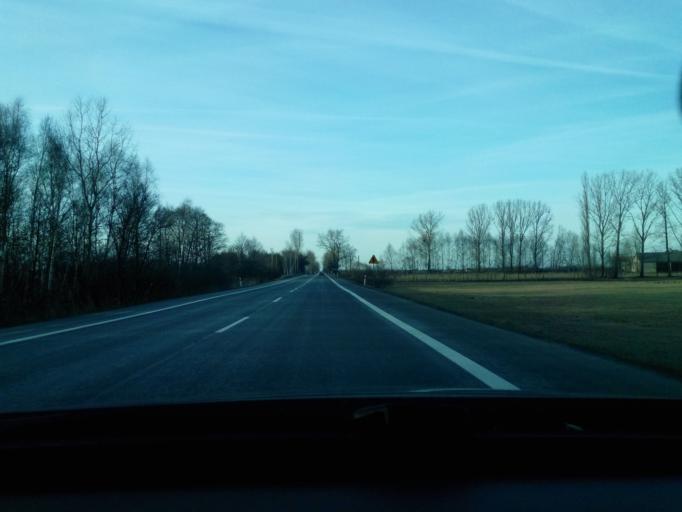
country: PL
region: Kujawsko-Pomorskie
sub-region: Powiat wloclawski
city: Lubien Kujawski
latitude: 52.4236
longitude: 19.1643
